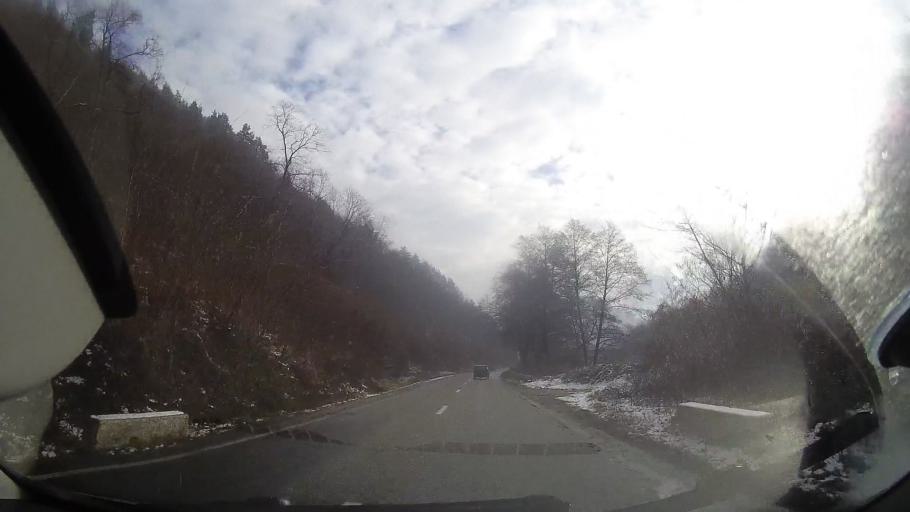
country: RO
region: Alba
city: Salciua de Sus
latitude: 46.3986
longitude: 23.3811
